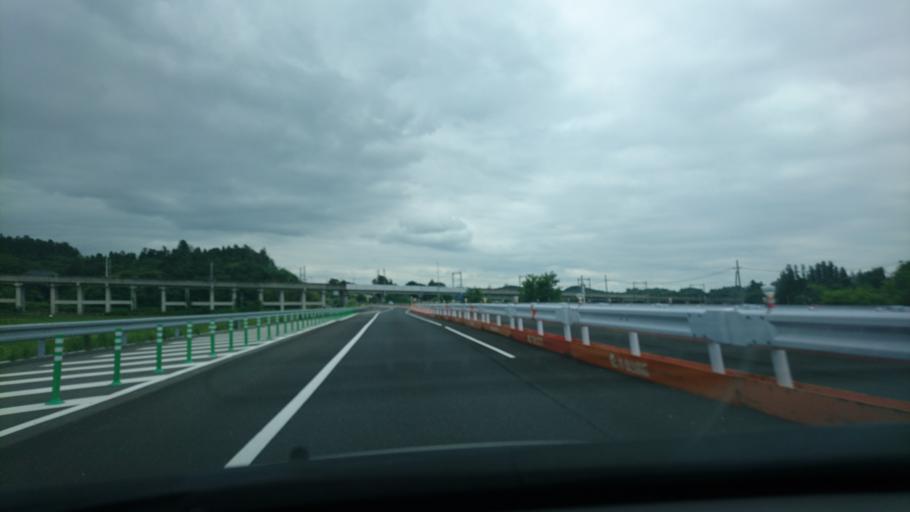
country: JP
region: Miyagi
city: Kogota
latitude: 38.7303
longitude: 141.0576
